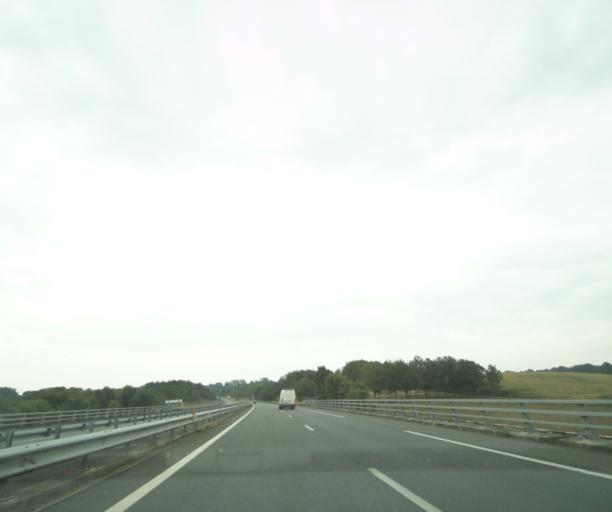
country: FR
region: Pays de la Loire
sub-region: Departement de la Vendee
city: Bournezeau
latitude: 46.6632
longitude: -1.1570
